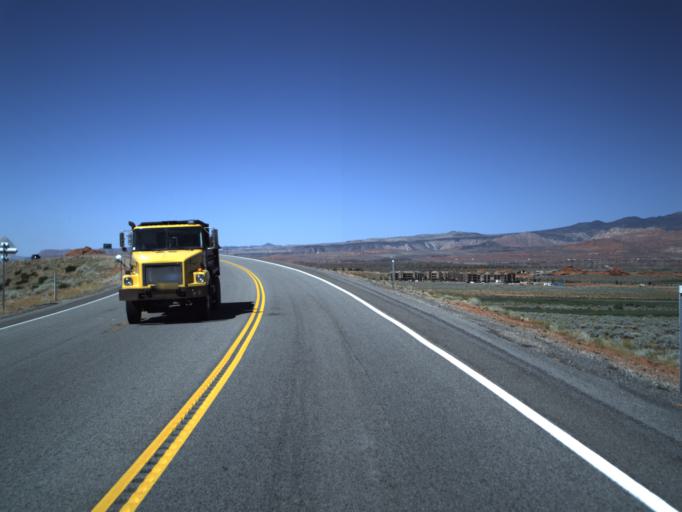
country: US
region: Utah
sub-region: Washington County
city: Washington
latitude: 37.1073
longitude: -113.3973
